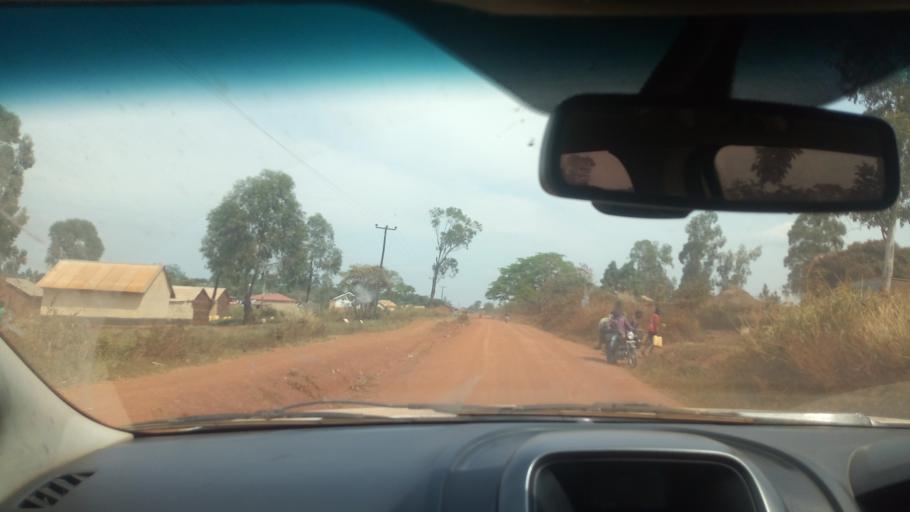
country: UG
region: Western Region
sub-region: Kiryandongo District
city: Kiryandongo
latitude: 1.9417
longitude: 32.1622
